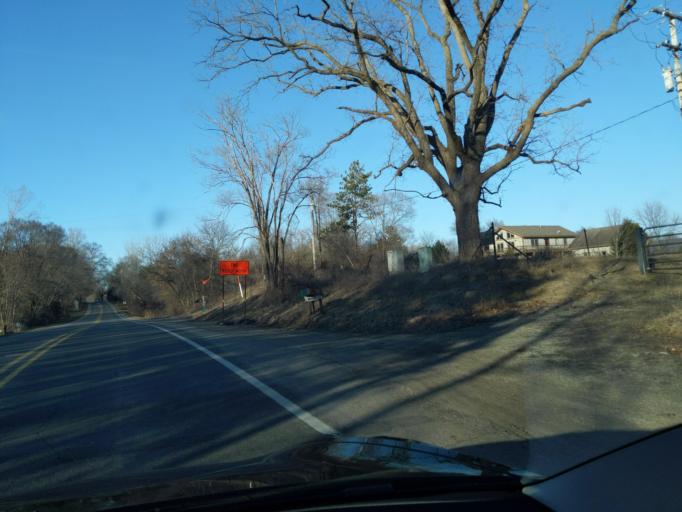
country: US
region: Michigan
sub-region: Washtenaw County
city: Chelsea
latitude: 42.3379
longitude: -84.0282
